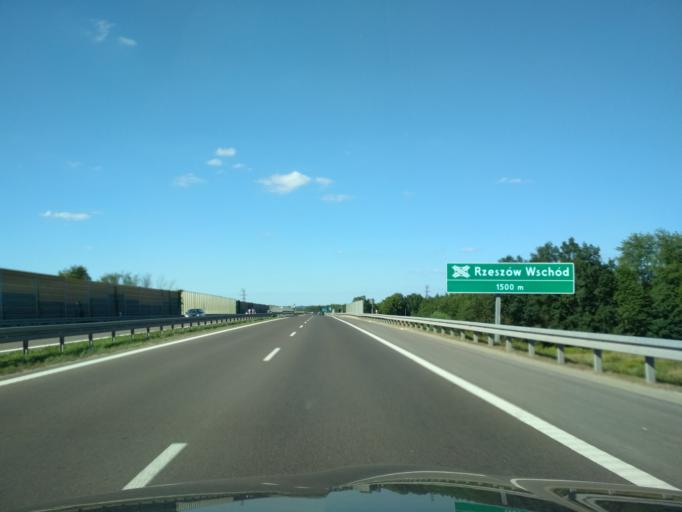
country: PL
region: Subcarpathian Voivodeship
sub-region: Powiat rzeszowski
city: Trzebownisko
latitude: 50.0751
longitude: 22.0584
